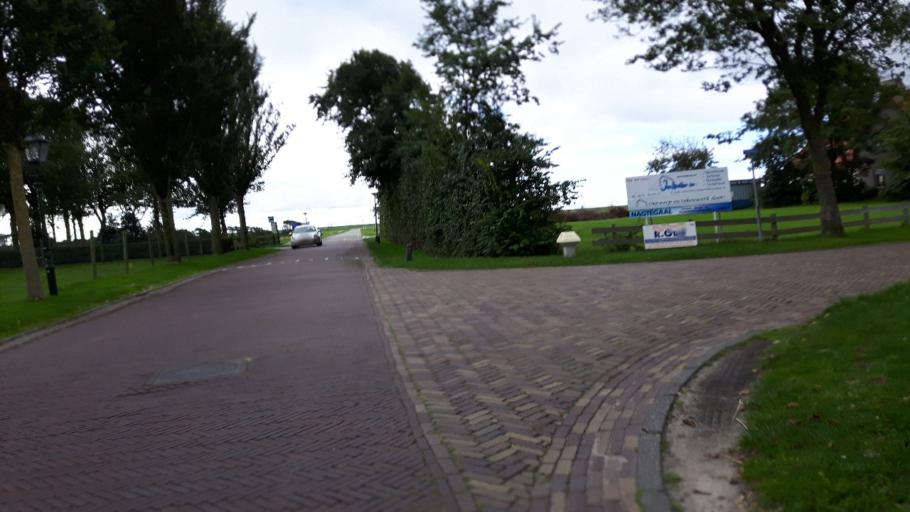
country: NL
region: Friesland
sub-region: Gemeente Ameland
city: Hollum
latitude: 53.4423
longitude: 5.6867
